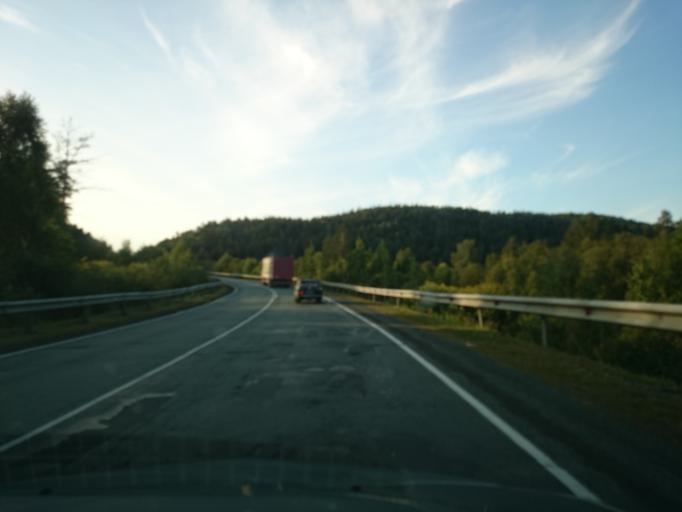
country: RU
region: Bashkortostan
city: Inzer
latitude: 53.9703
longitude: 57.8755
